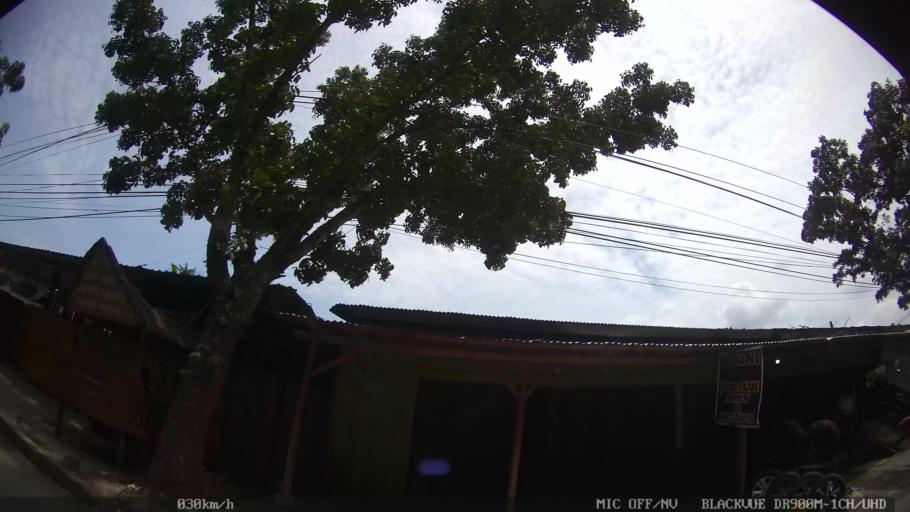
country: ID
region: North Sumatra
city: Sunggal
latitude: 3.5409
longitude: 98.6374
